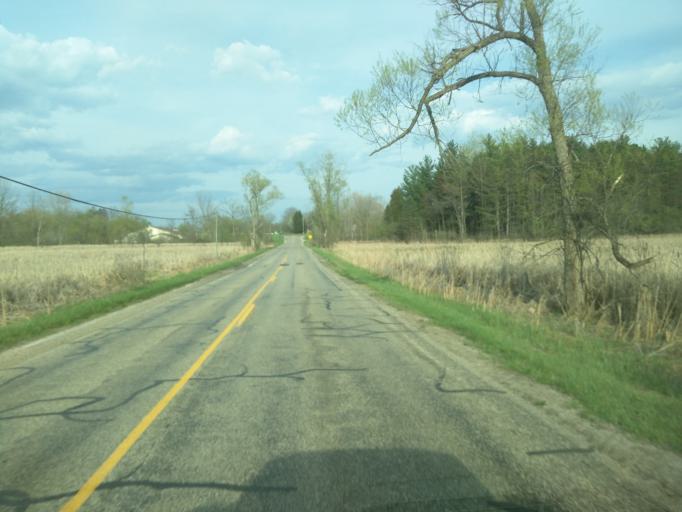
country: US
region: Michigan
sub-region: Eaton County
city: Dimondale
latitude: 42.6257
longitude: -84.6275
